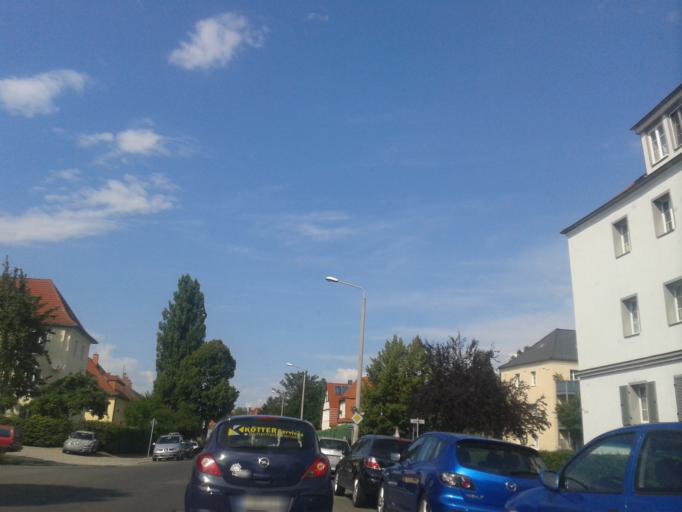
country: DE
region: Saxony
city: Dresden
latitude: 51.0204
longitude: 13.7589
